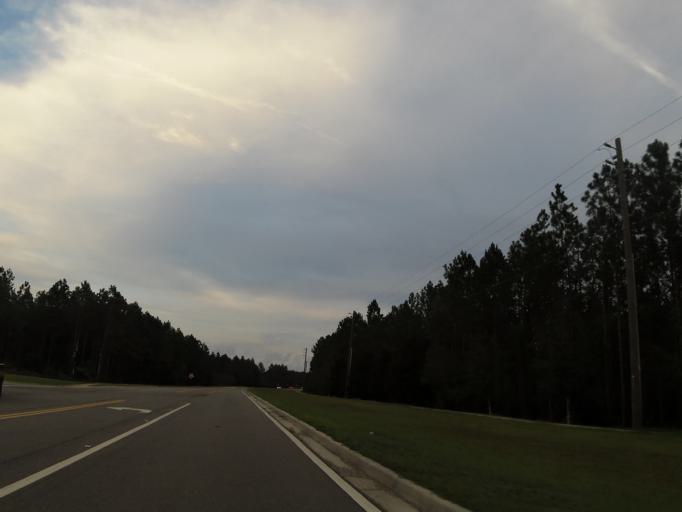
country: US
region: Florida
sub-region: Saint Johns County
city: Fruit Cove
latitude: 30.0857
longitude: -81.5723
